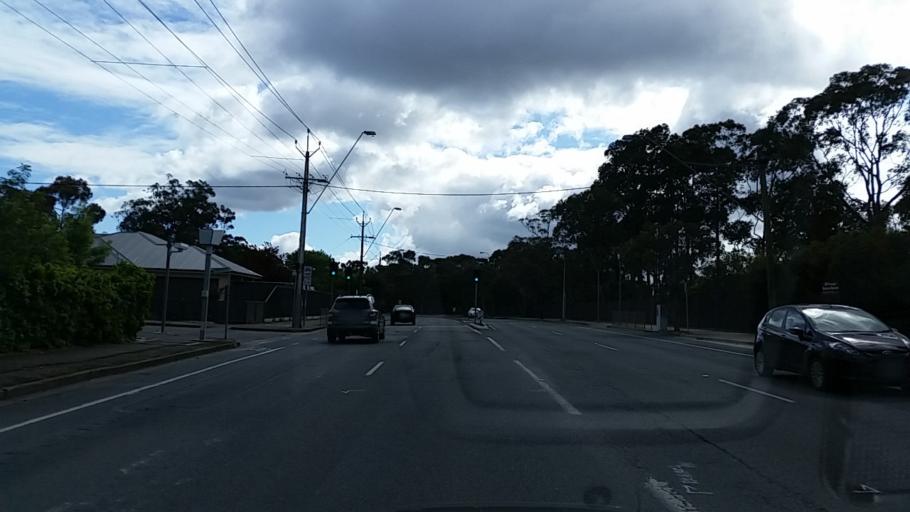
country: AU
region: South Australia
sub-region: Mitcham
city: Blackwood
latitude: -35.0238
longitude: 138.6067
